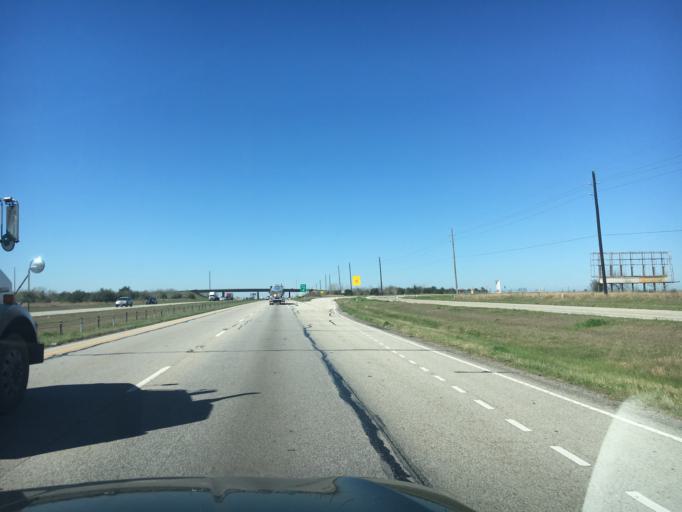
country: US
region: Texas
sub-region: Austin County
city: Sealy
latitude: 29.7531
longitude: -96.2655
